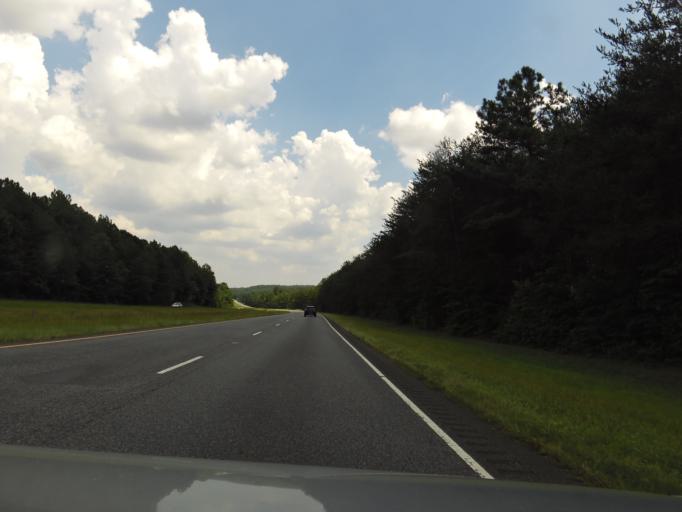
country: US
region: North Carolina
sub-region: Polk County
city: Columbus
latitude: 35.2699
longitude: -82.1542
